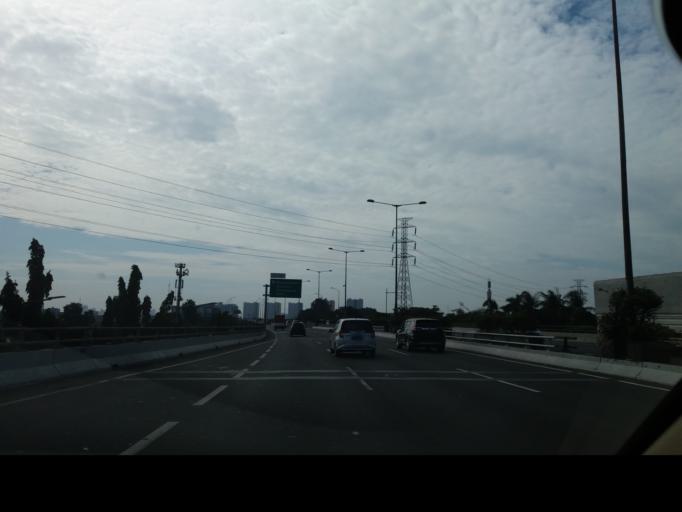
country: ID
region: Jakarta Raya
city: Jakarta
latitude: -6.2063
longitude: 106.8737
